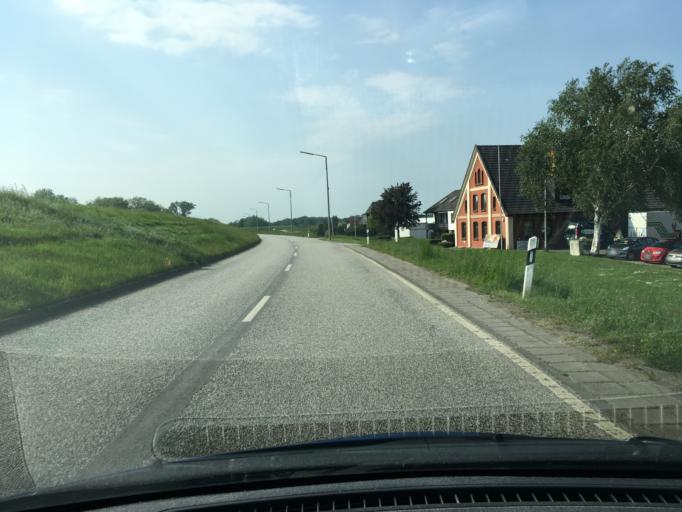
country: DE
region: Hamburg
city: Rothenburgsort
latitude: 53.4665
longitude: 10.0551
